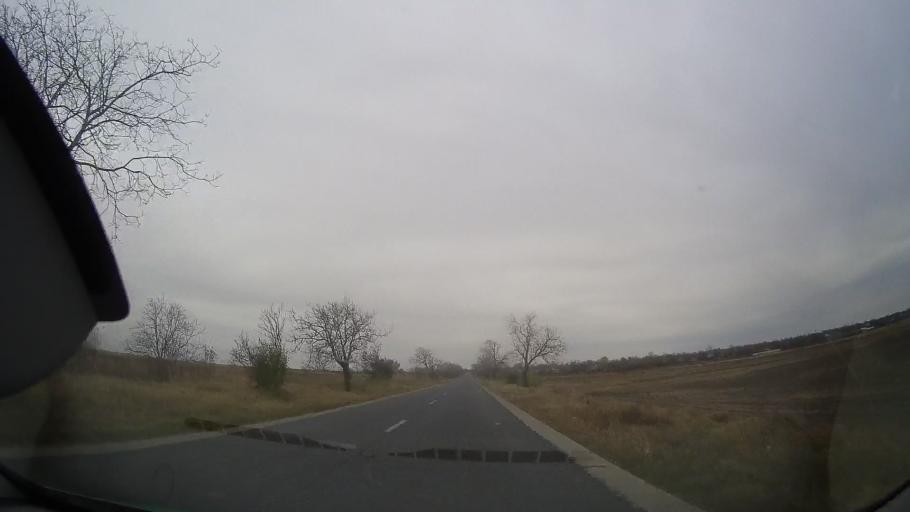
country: RO
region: Braila
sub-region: Comuna Ciocile
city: Ciocile
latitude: 44.7756
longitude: 27.1715
